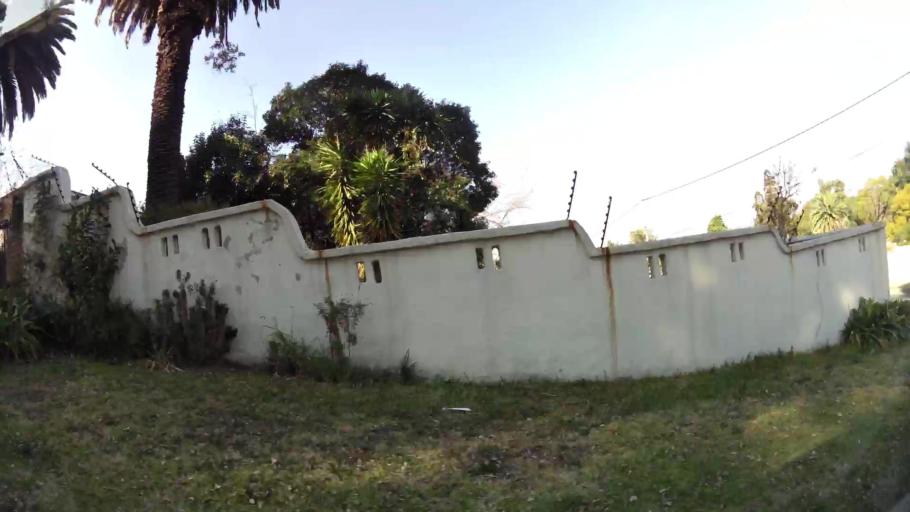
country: ZA
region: Gauteng
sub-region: City of Johannesburg Metropolitan Municipality
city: Johannesburg
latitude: -26.1809
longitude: 28.0828
